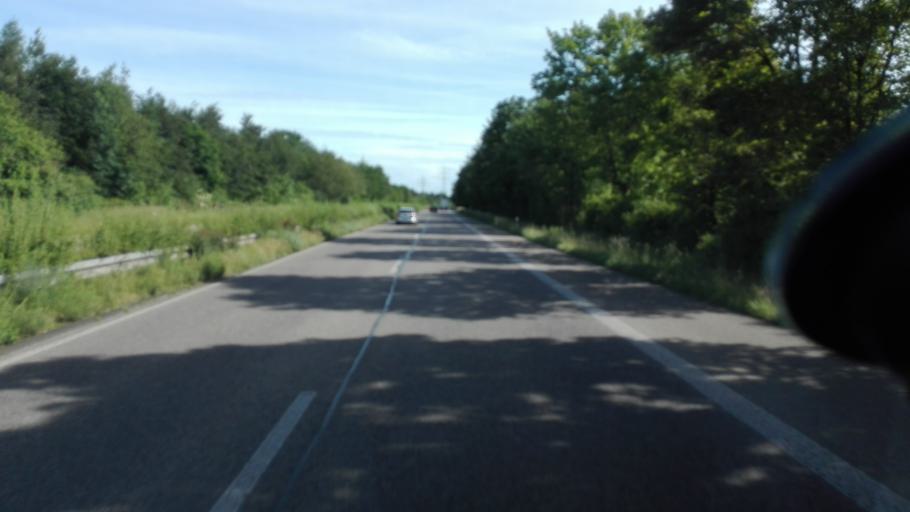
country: DE
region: Baden-Wuerttemberg
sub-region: Karlsruhe Region
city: Eggenstein-Leopoldshafen
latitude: 49.0787
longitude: 8.4080
